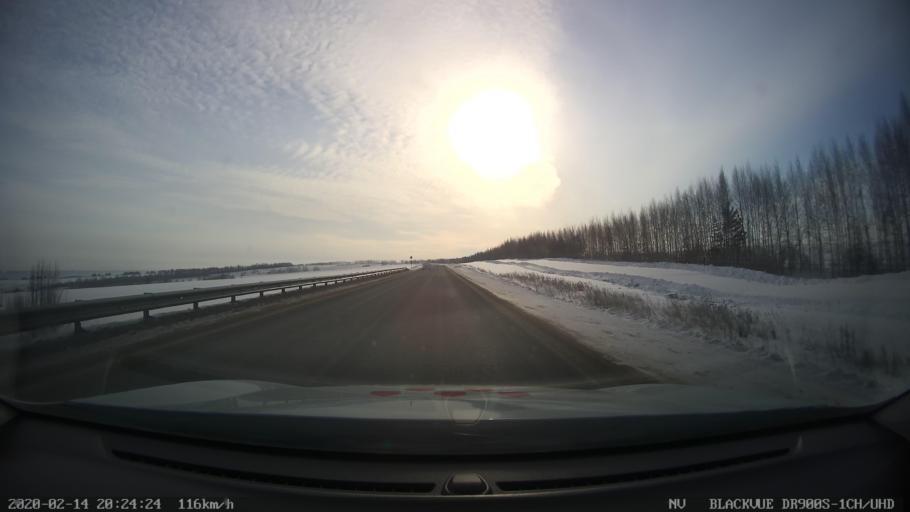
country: RU
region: Tatarstan
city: Verkhniy Uslon
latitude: 55.5130
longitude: 48.9695
